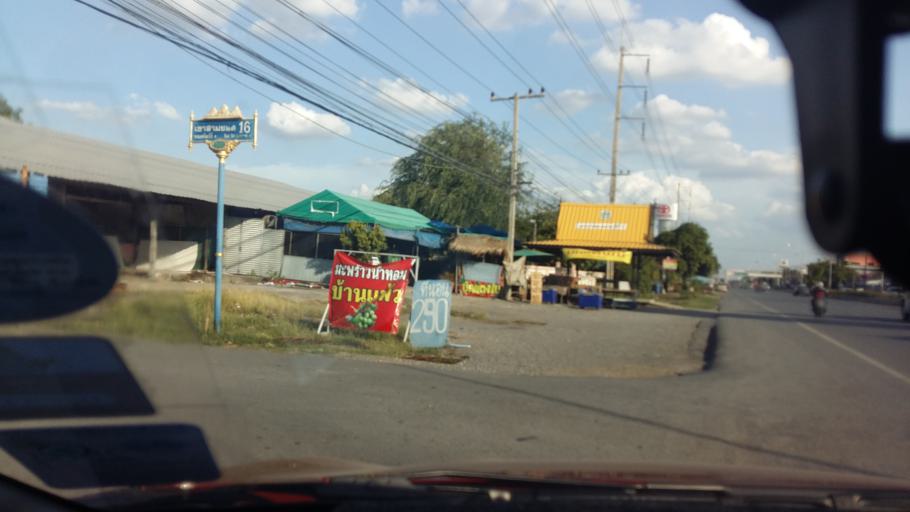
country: TH
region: Lop Buri
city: Lop Buri
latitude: 14.8309
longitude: 100.6463
